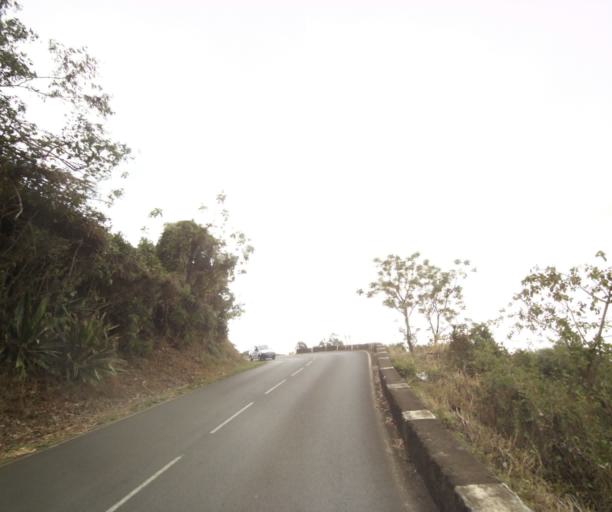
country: RE
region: Reunion
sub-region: Reunion
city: Trois-Bassins
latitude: -21.0648
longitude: 55.2796
